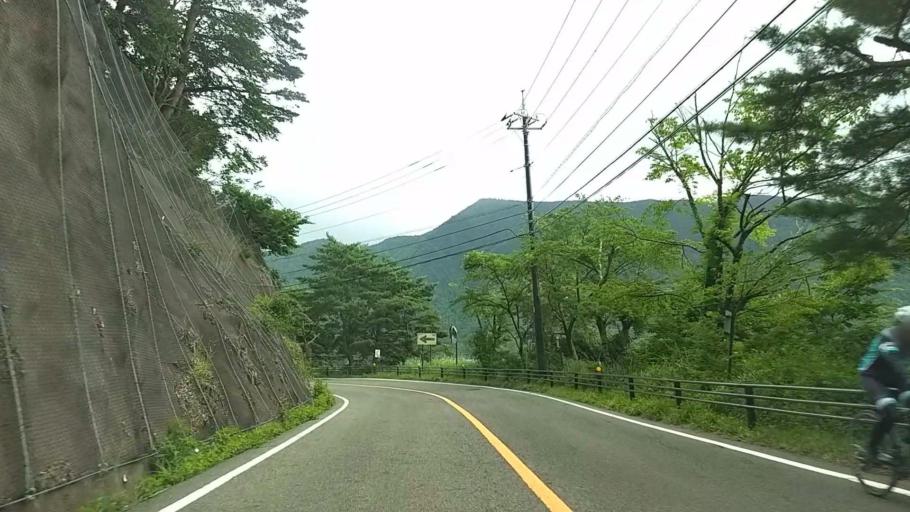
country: JP
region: Yamanashi
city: Fujikawaguchiko
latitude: 35.5041
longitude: 138.6900
